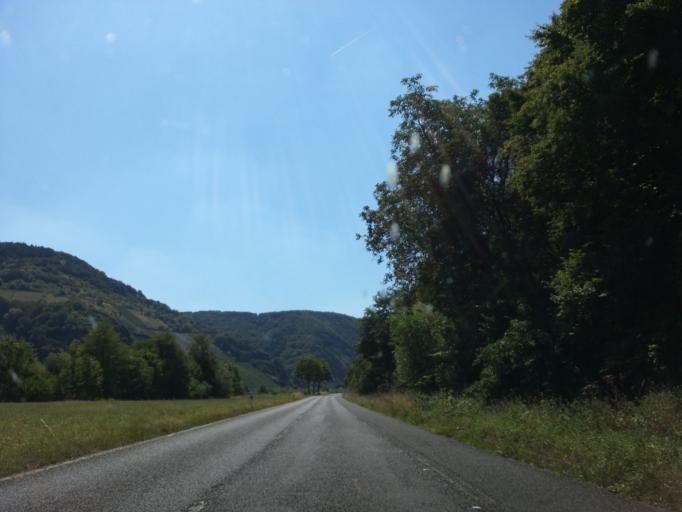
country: DE
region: Rheinland-Pfalz
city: Wintrich
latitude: 49.8784
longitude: 6.9453
